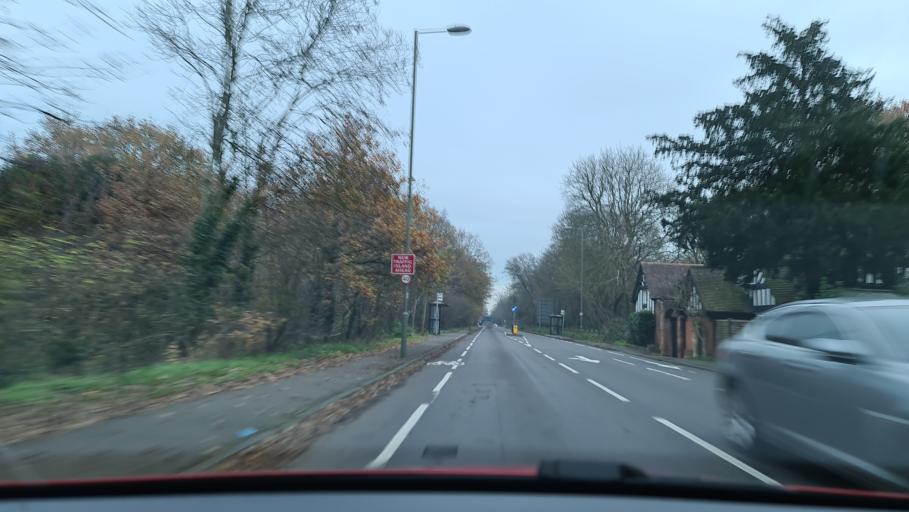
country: GB
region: England
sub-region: Surrey
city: Hinchley Wood
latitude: 51.3789
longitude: -0.3474
